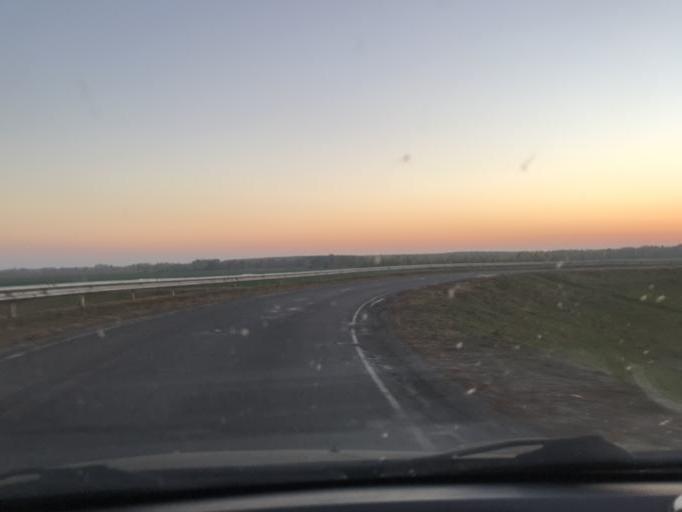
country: BY
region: Gomel
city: Horad Rechytsa
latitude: 52.2904
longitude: 30.4669
